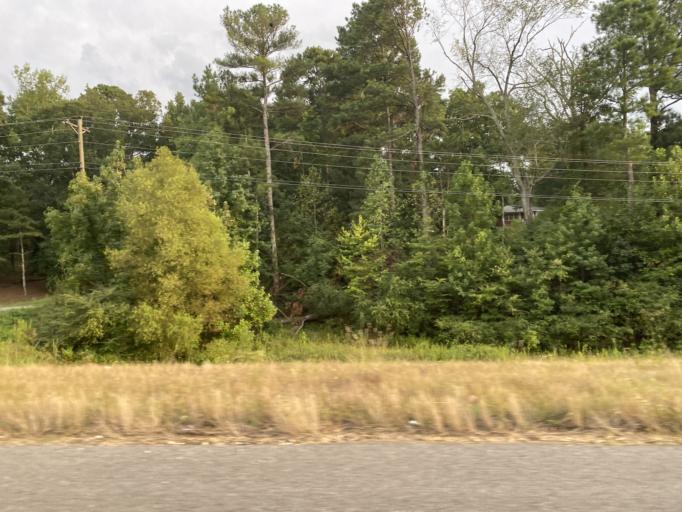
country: US
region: Alabama
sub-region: Franklin County
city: Red Bay
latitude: 34.4492
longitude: -88.0698
